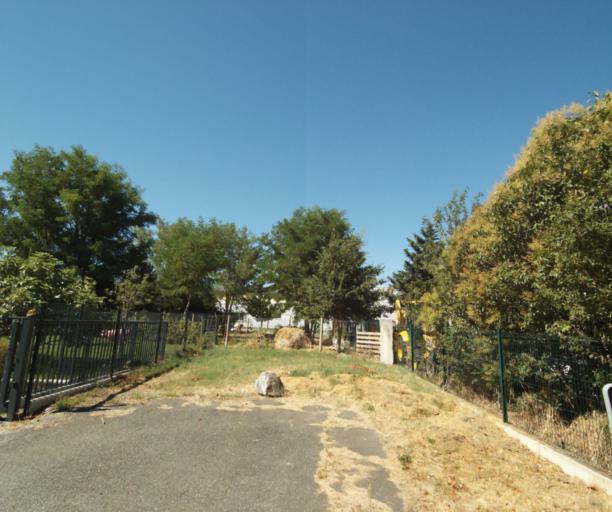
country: FR
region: Midi-Pyrenees
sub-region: Departement de la Haute-Garonne
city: Pechabou
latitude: 43.5122
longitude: 1.5207
